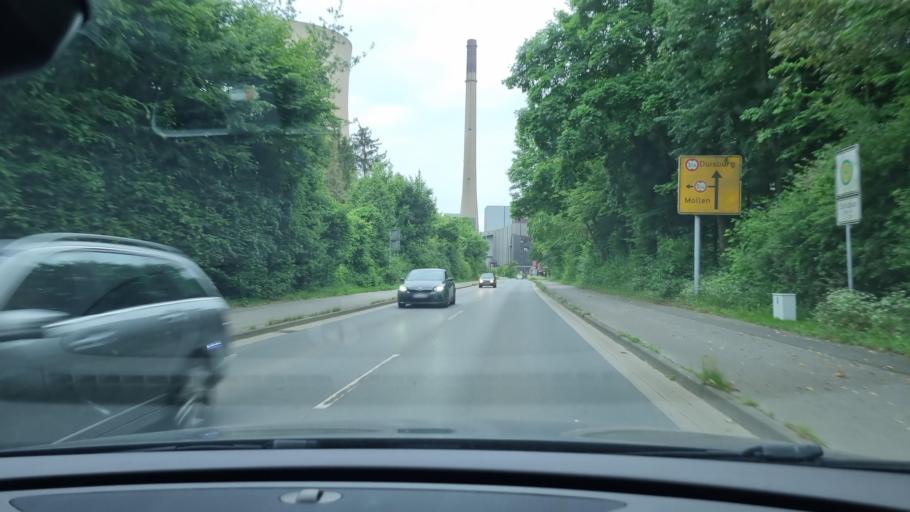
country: DE
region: North Rhine-Westphalia
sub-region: Regierungsbezirk Dusseldorf
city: Voerde
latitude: 51.5812
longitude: 6.6796
